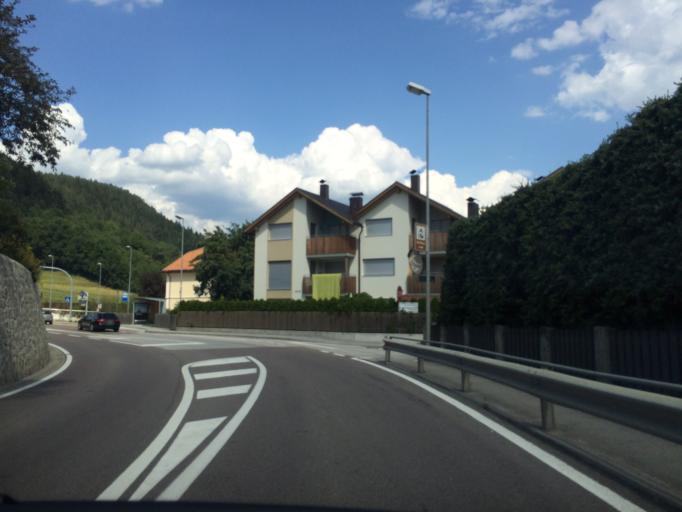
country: IT
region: Trentino-Alto Adige
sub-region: Bolzano
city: San Lorenzo di Sebato
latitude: 46.7833
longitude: 11.8953
